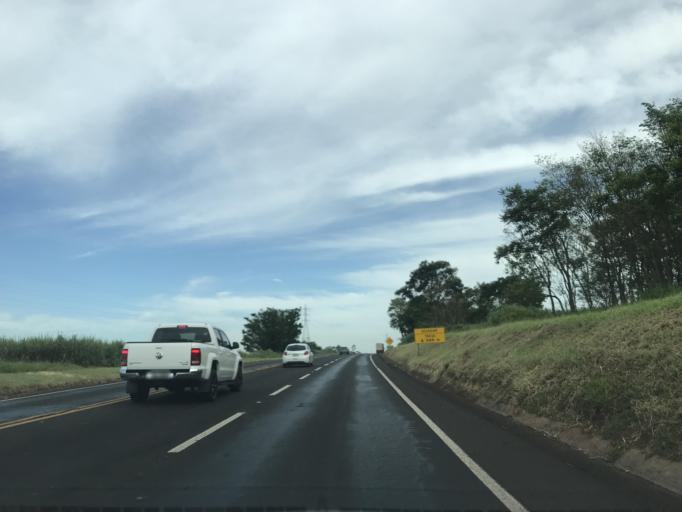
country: BR
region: Parana
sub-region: Paranavai
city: Nova Aurora
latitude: -22.9942
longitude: -52.5887
